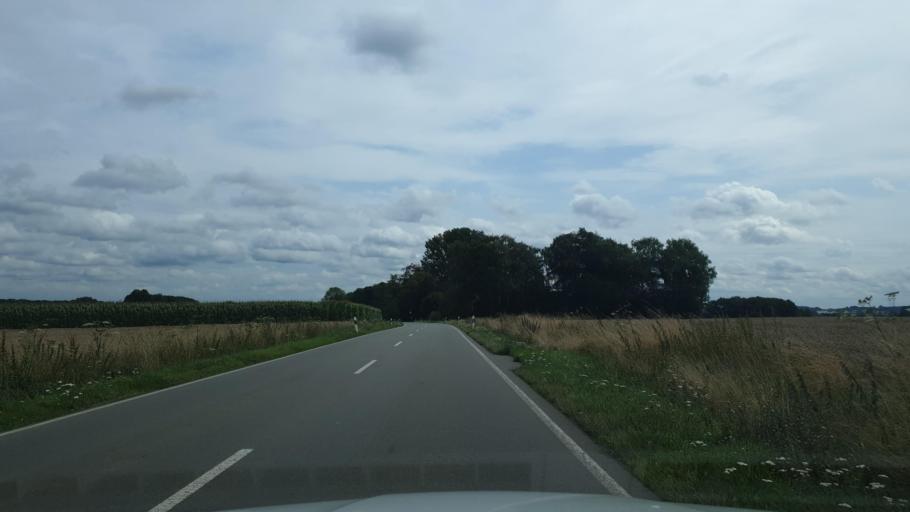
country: DE
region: Lower Saxony
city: Dissen
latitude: 52.1826
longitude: 8.2210
